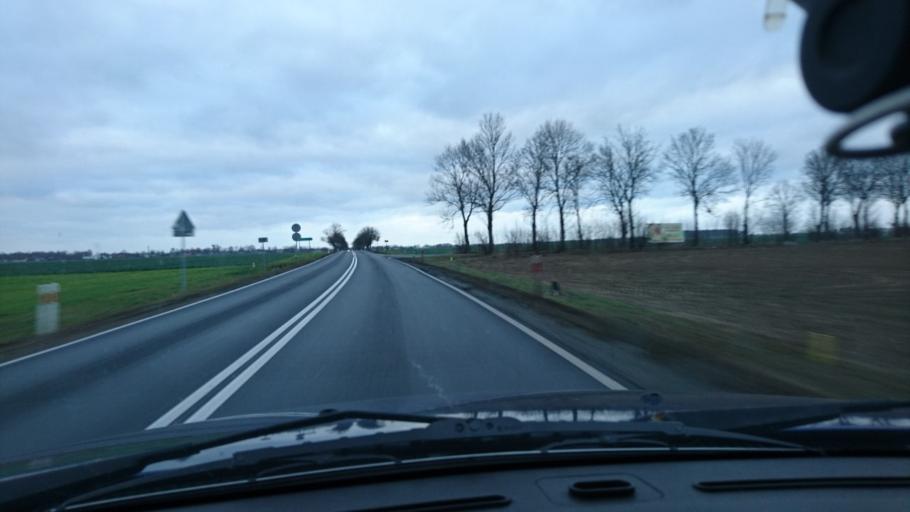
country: PL
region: Opole Voivodeship
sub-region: Powiat kluczborski
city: Byczyna
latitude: 51.0698
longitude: 18.2038
